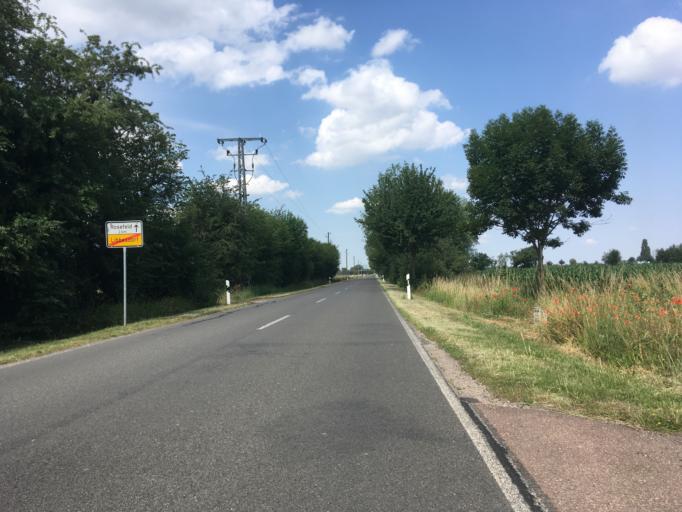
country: DE
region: Saxony-Anhalt
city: Quellendorf
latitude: 51.7735
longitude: 12.1036
